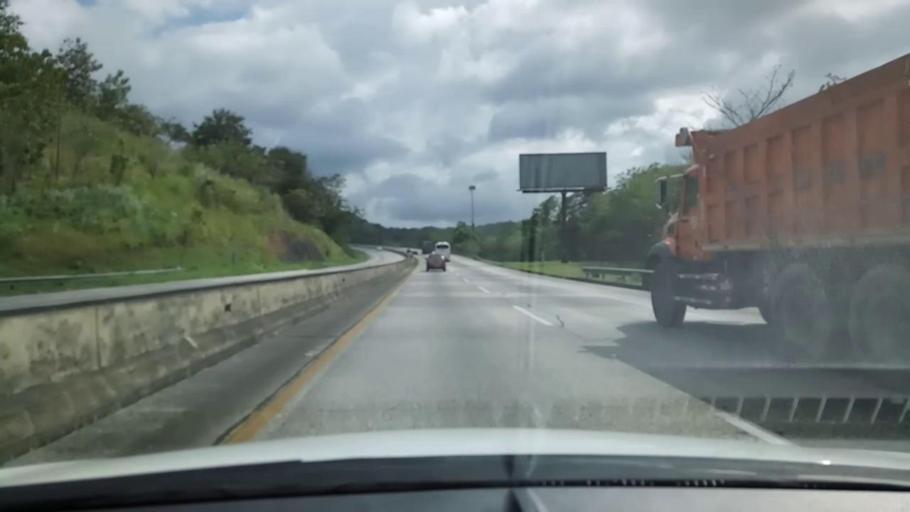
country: PA
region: Panama
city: Chilibre
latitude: 9.1317
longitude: -79.6224
